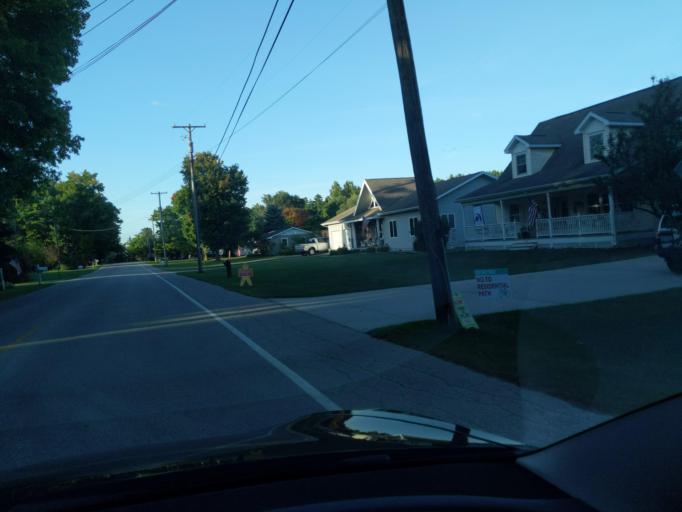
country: US
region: Michigan
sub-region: Antrim County
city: Elk Rapids
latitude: 44.8900
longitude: -85.4223
